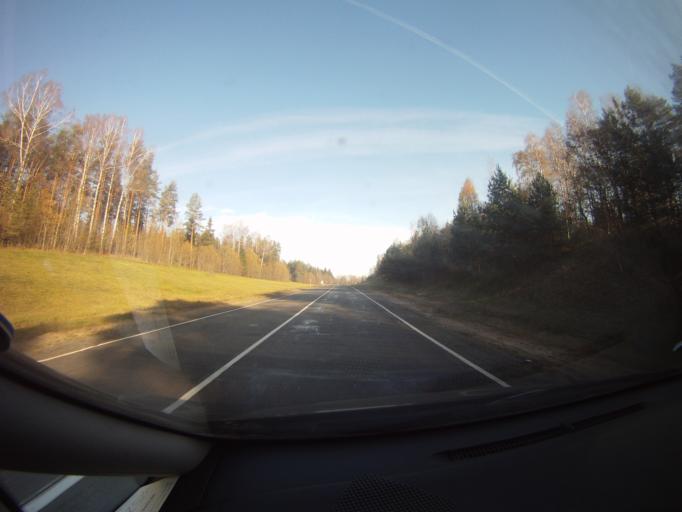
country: BY
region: Minsk
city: Syomkava
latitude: 54.2439
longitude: 27.4853
